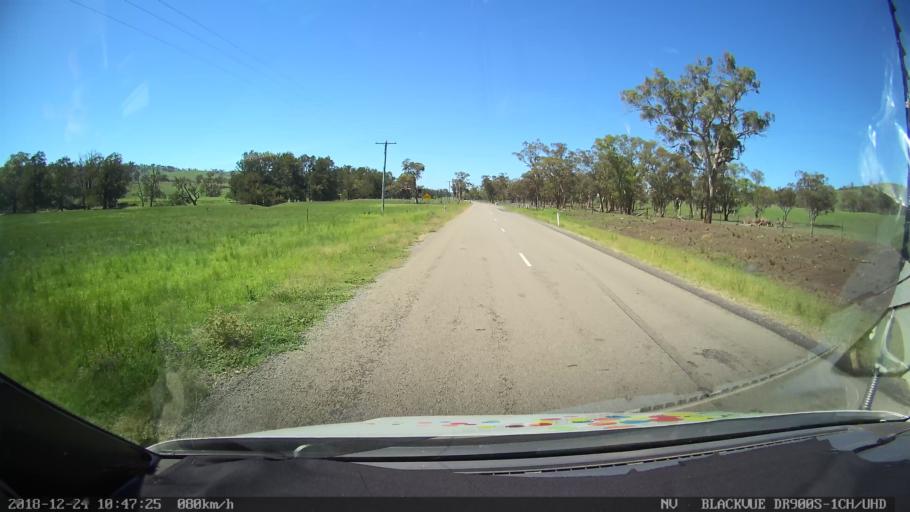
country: AU
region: New South Wales
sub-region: Upper Hunter Shire
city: Merriwa
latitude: -31.9242
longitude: 150.4296
